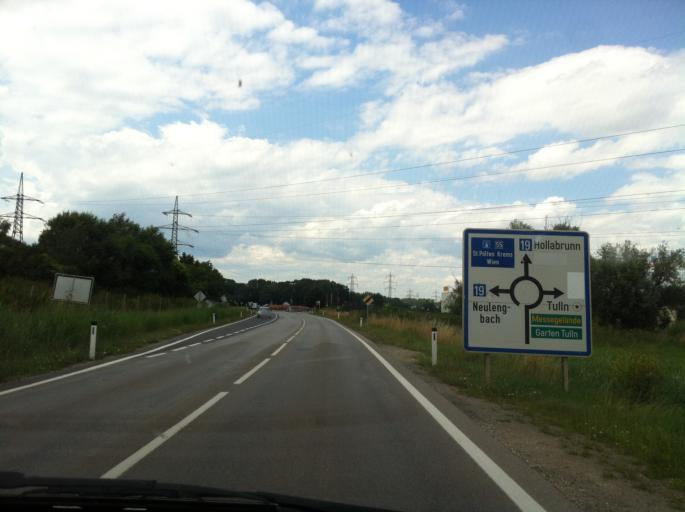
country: AT
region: Lower Austria
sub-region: Politischer Bezirk Tulln
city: Langenrohr
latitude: 48.3218
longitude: 16.0286
